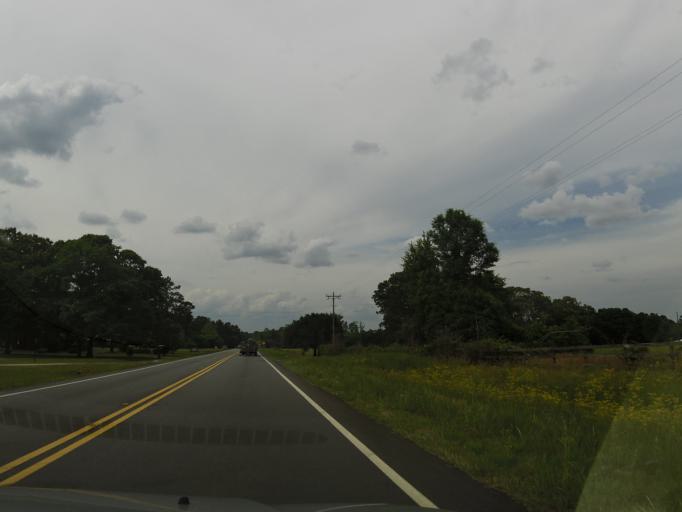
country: US
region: Georgia
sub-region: McDuffie County
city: Thomson
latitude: 33.4111
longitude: -82.4811
